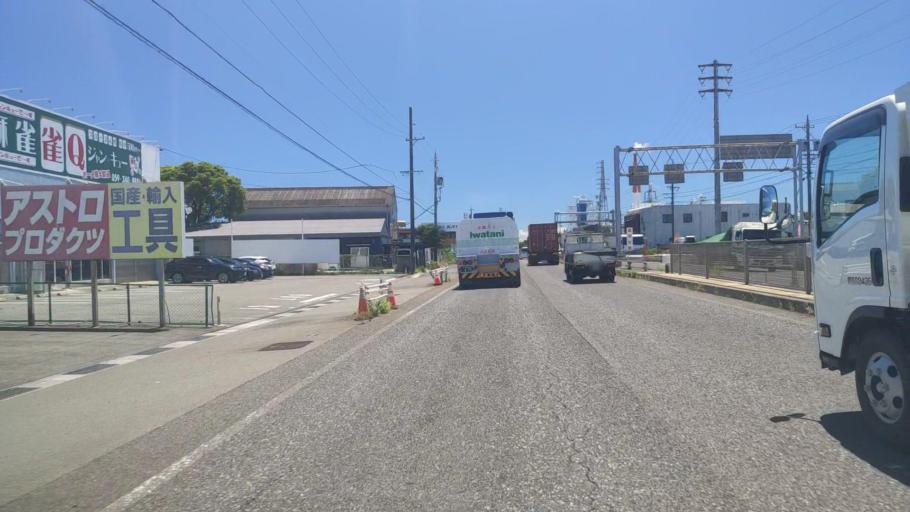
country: JP
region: Mie
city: Yokkaichi
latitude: 34.9388
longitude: 136.6168
